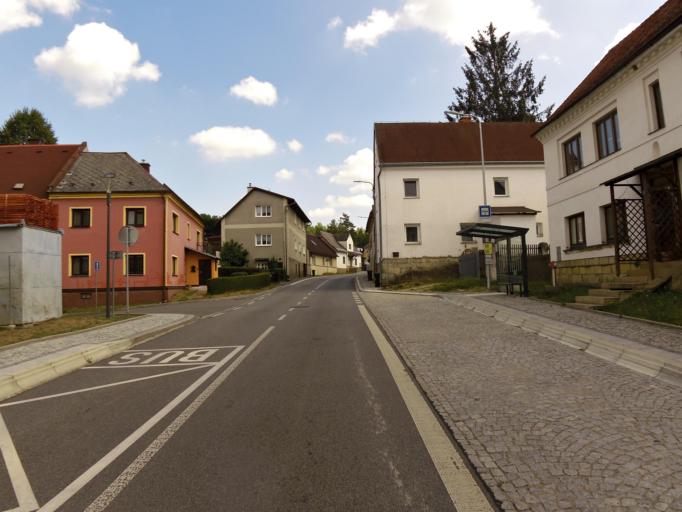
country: CZ
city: Osecna
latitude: 50.6943
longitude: 14.9214
